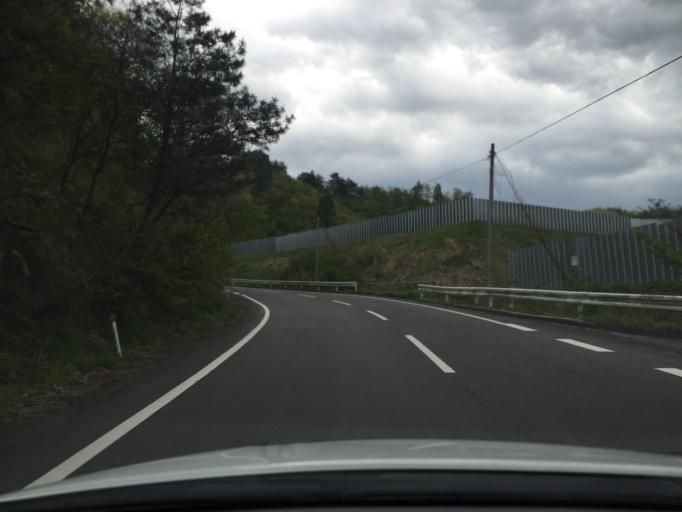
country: JP
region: Fukushima
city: Yanagawamachi-saiwaicho
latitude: 37.7528
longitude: 140.6909
